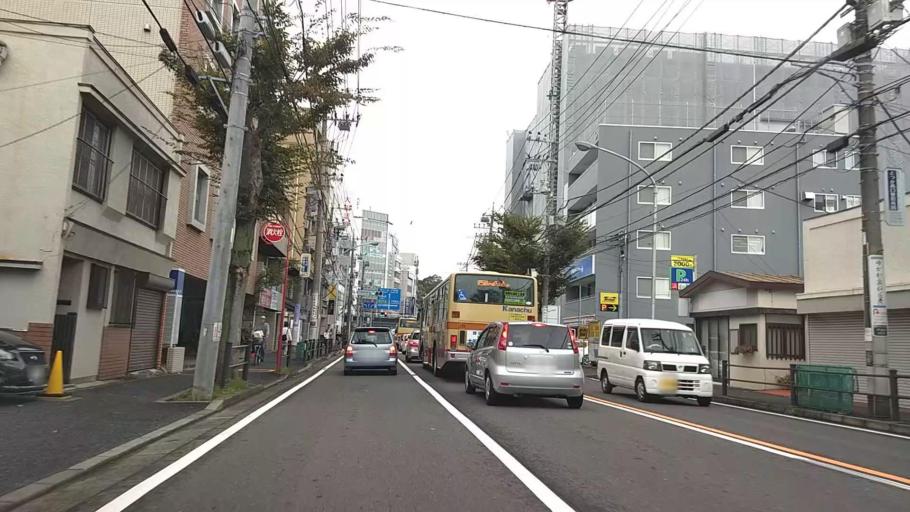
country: JP
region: Kanagawa
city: Fujisawa
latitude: 35.3990
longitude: 139.5310
